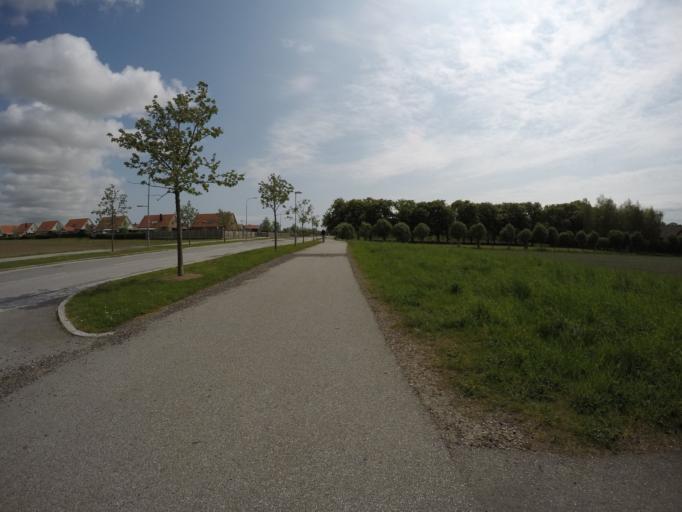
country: SE
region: Skane
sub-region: Malmo
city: Tygelsjo
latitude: 55.5239
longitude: 12.9966
